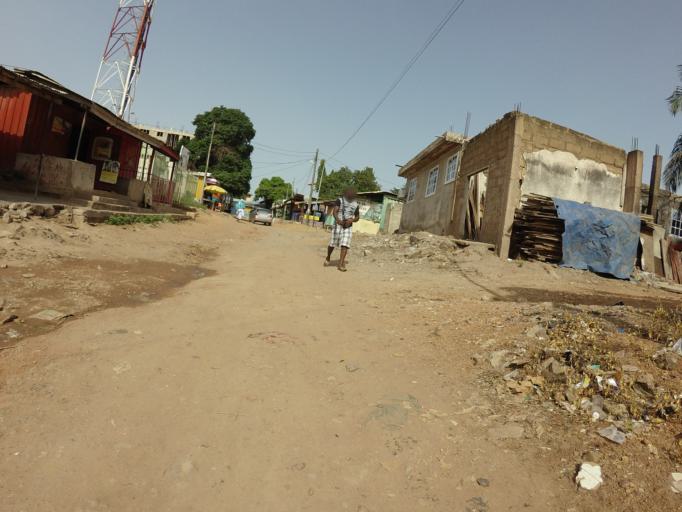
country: GH
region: Greater Accra
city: Dome
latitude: 5.6142
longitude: -0.2410
